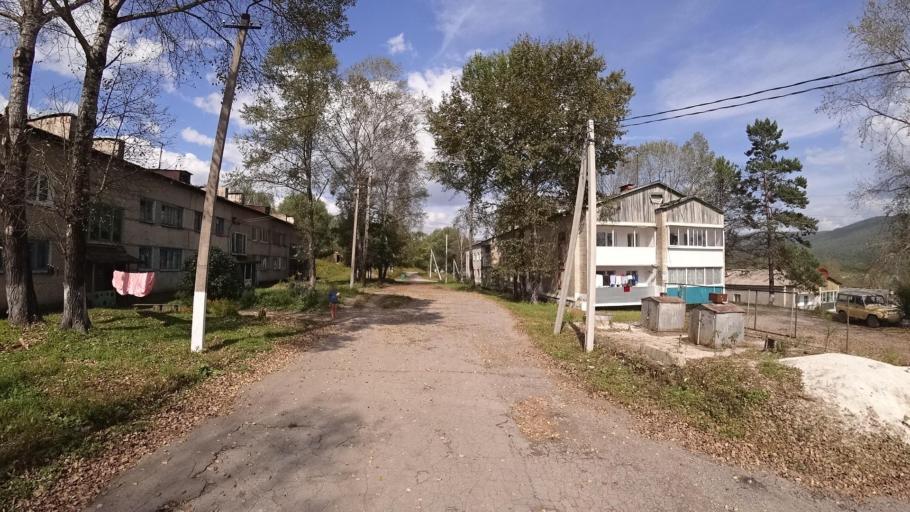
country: RU
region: Jewish Autonomous Oblast
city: Londoko
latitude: 49.0242
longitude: 131.9225
